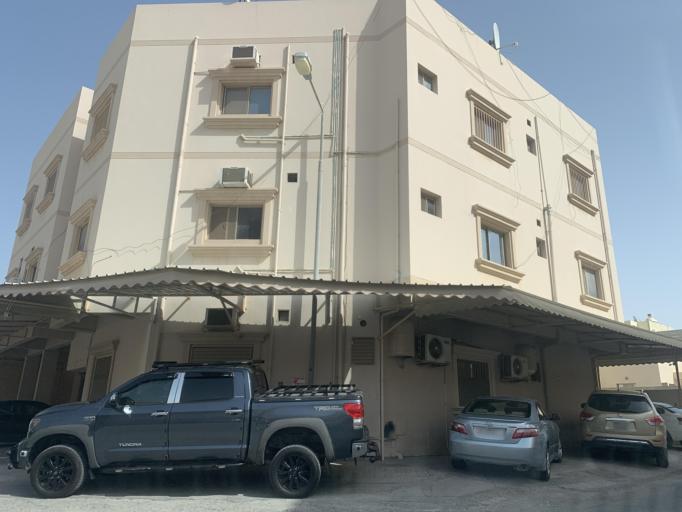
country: BH
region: Northern
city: Ar Rifa'
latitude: 26.1463
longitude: 50.5682
